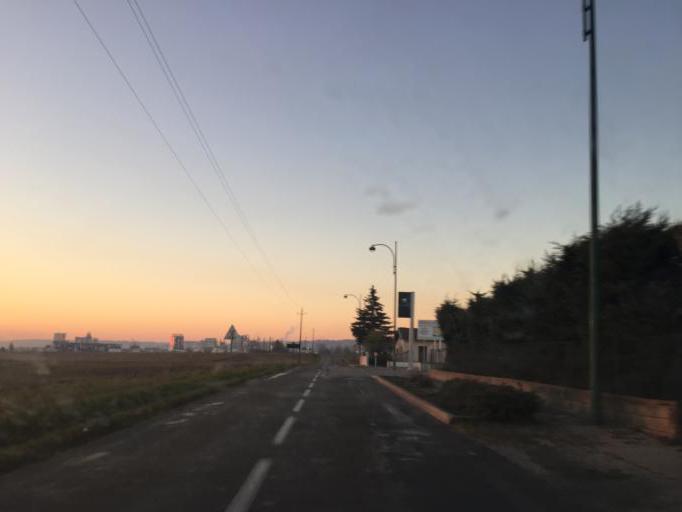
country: FR
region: Rhone-Alpes
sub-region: Departement de l'Ain
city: Balan
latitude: 45.8427
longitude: 5.1108
